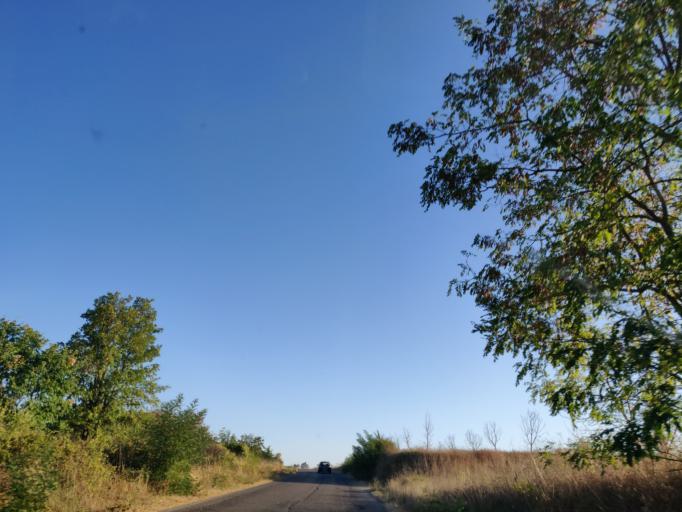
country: IT
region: Latium
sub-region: Provincia di Viterbo
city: Grotte di Castro
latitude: 42.6953
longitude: 11.8782
